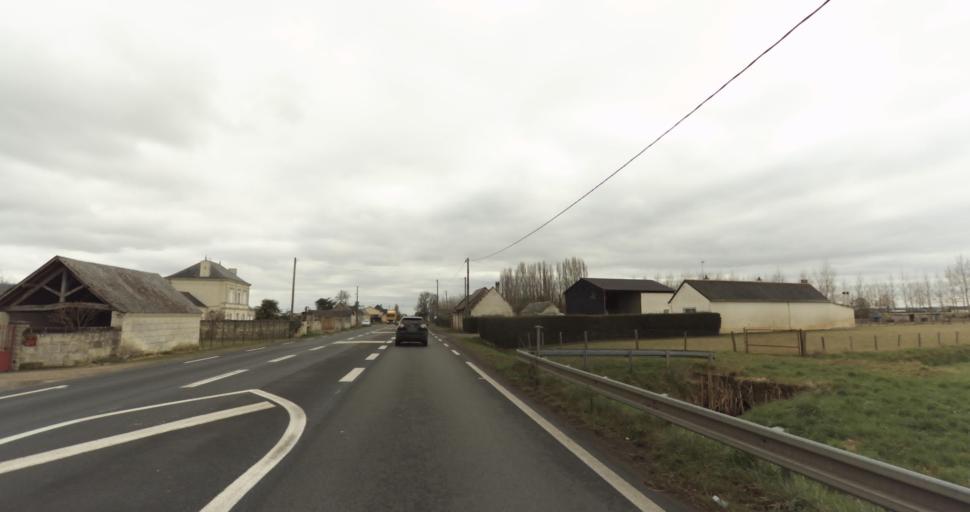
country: FR
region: Pays de la Loire
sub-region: Departement de Maine-et-Loire
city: Vivy
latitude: 47.3216
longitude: -0.0519
